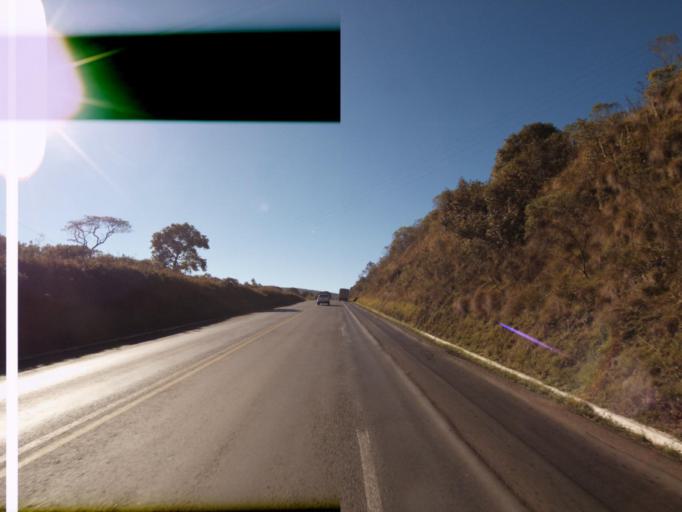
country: BR
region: Santa Catarina
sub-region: Concordia
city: Concordia
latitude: -26.8886
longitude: -51.9940
